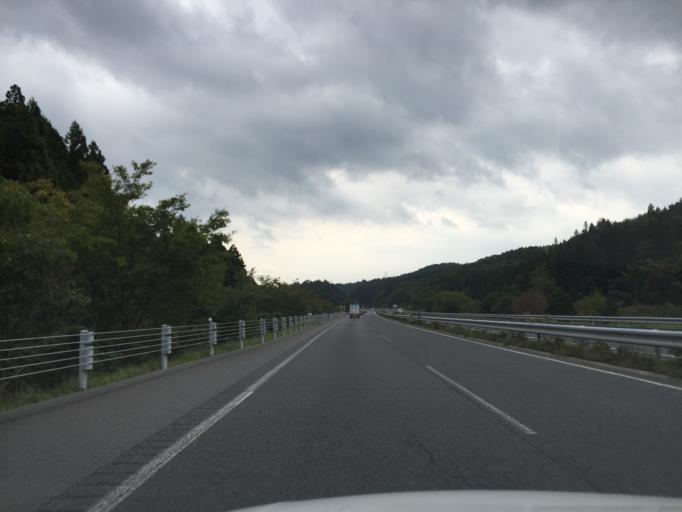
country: JP
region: Fukushima
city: Iwaki
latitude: 37.1914
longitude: 140.7069
